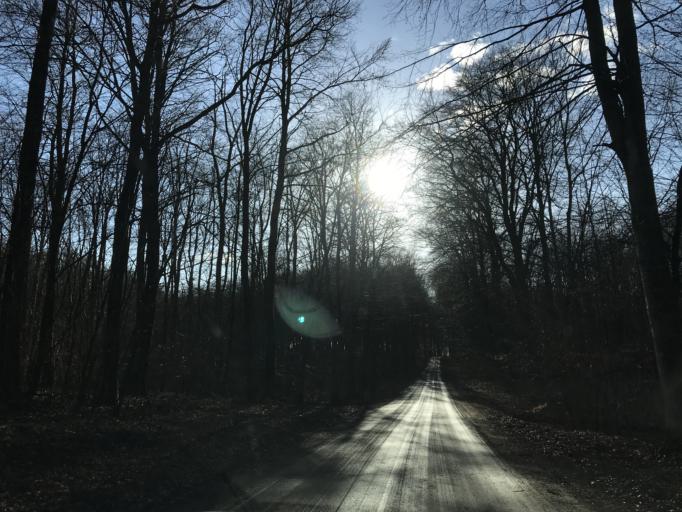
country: SE
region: Skane
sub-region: Ystads Kommun
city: Ystad
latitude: 55.5592
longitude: 13.8217
